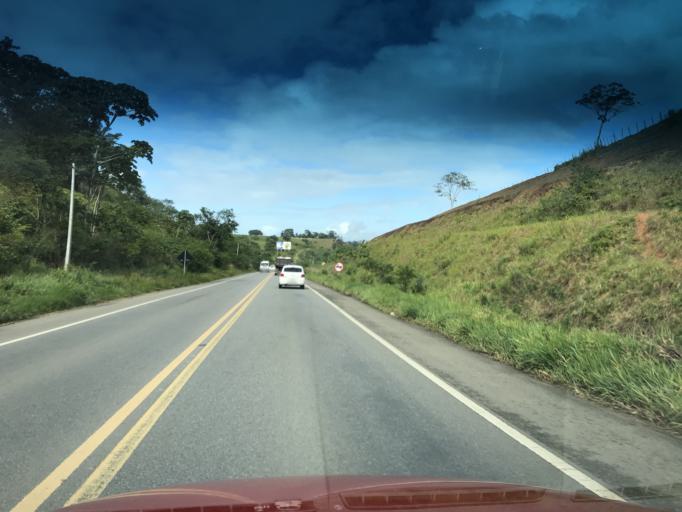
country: BR
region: Bahia
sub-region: Conceicao Do Almeida
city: Muritiba
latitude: -12.9050
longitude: -39.2379
